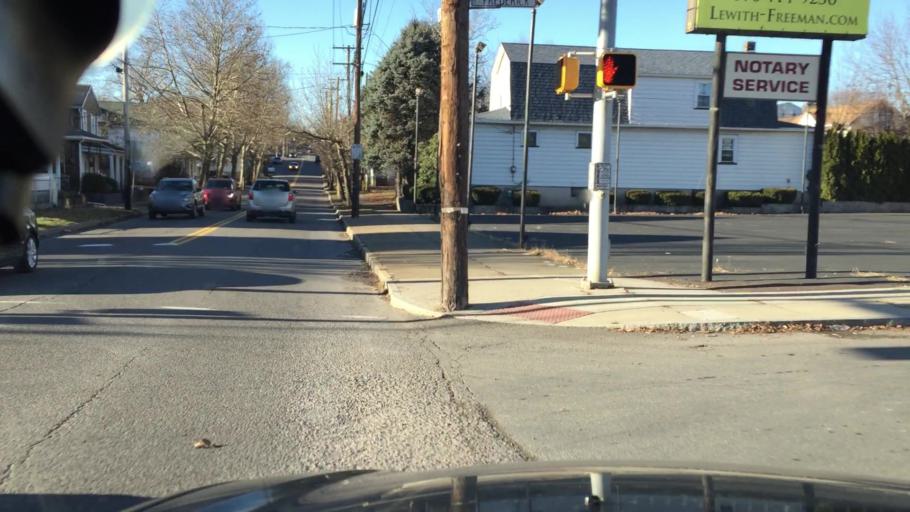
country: US
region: Pennsylvania
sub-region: Luzerne County
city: Ashley
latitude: 41.2255
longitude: -75.8908
